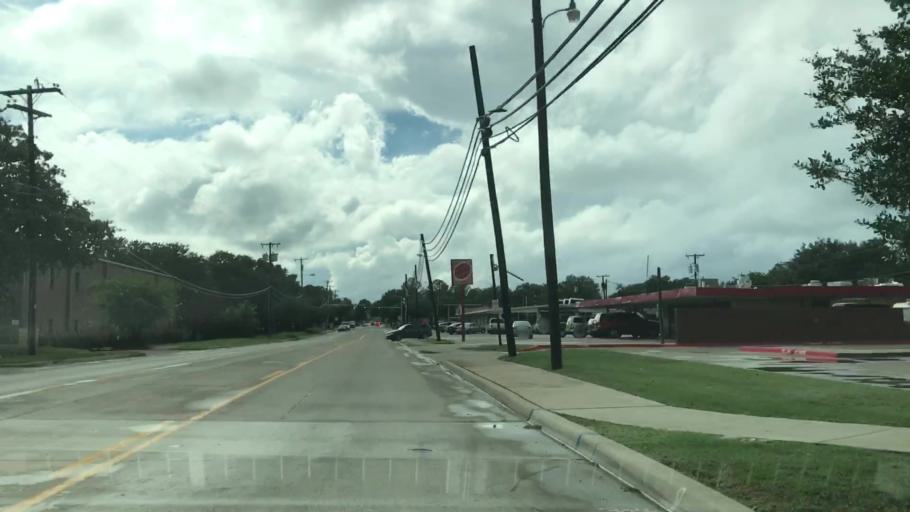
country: US
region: Texas
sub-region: Dallas County
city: Irving
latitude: 32.8297
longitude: -96.9280
